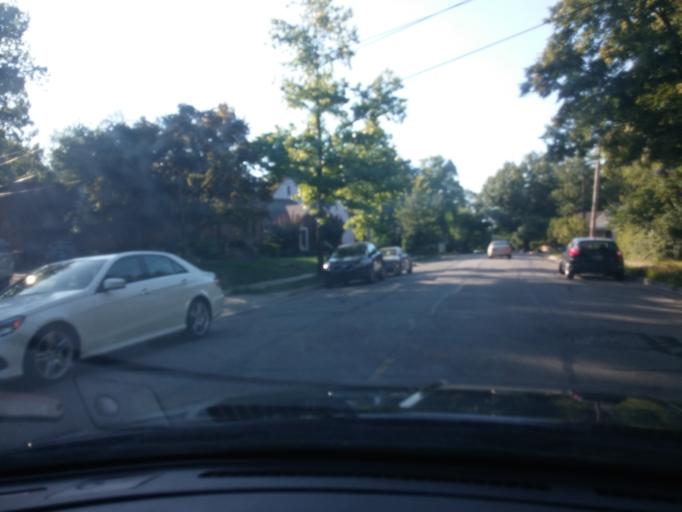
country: US
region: Indiana
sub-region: Tippecanoe County
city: West Lafayette
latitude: 40.4320
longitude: -86.9032
